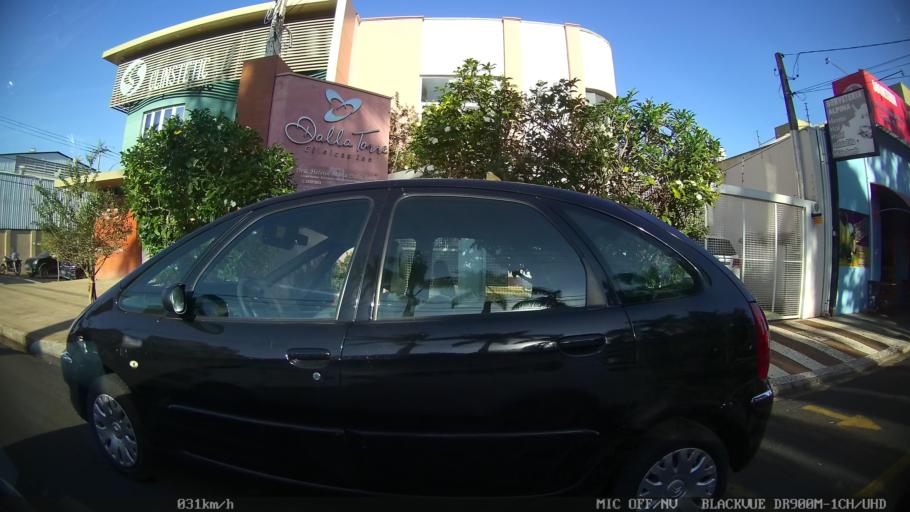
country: BR
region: Sao Paulo
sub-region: Sao Jose Do Rio Preto
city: Sao Jose do Rio Preto
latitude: -20.8072
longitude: -49.3871
